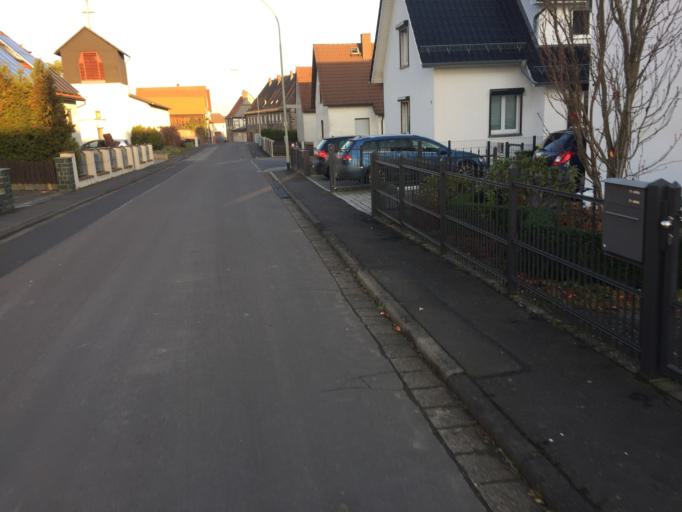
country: DE
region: Hesse
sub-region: Regierungsbezirk Darmstadt
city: Munzenberg
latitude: 50.4782
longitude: 8.7566
